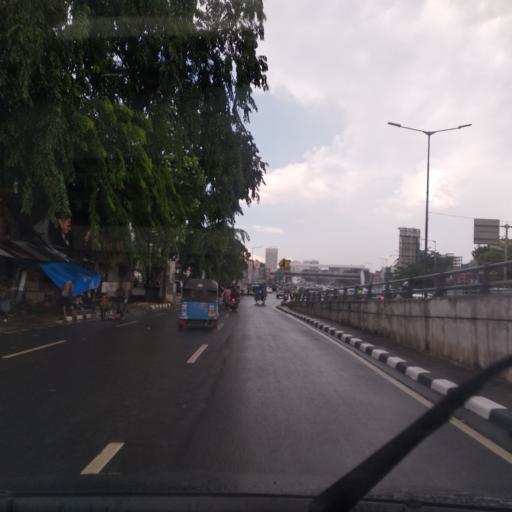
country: ID
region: Jakarta Raya
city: Jakarta
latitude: -6.2252
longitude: 106.8607
